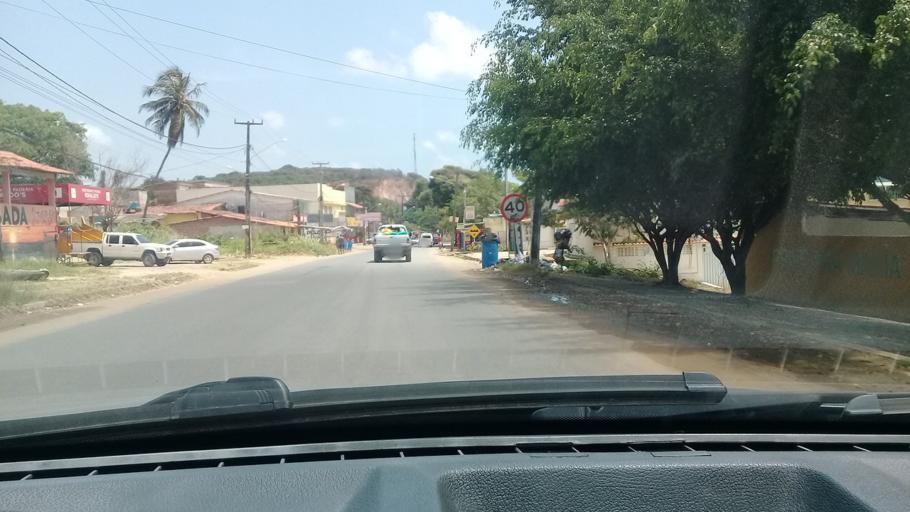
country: BR
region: Pernambuco
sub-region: Itamaraca
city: Itamaraca
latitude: -7.7879
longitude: -34.8405
